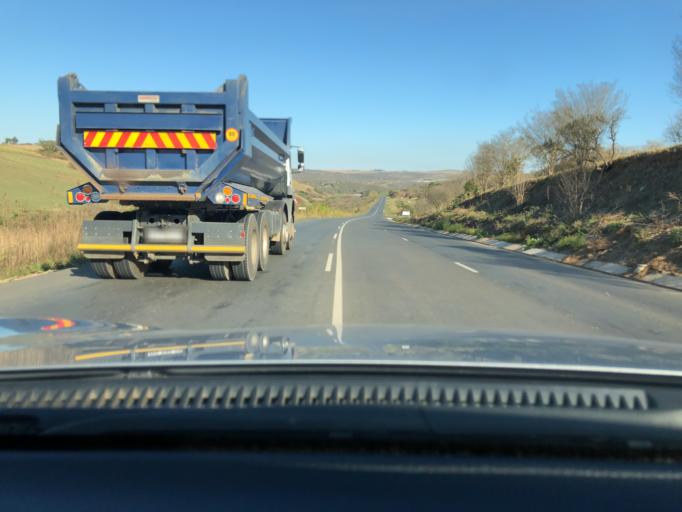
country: ZA
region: KwaZulu-Natal
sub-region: uMgungundlovu District Municipality
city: Camperdown
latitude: -29.7868
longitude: 30.5086
